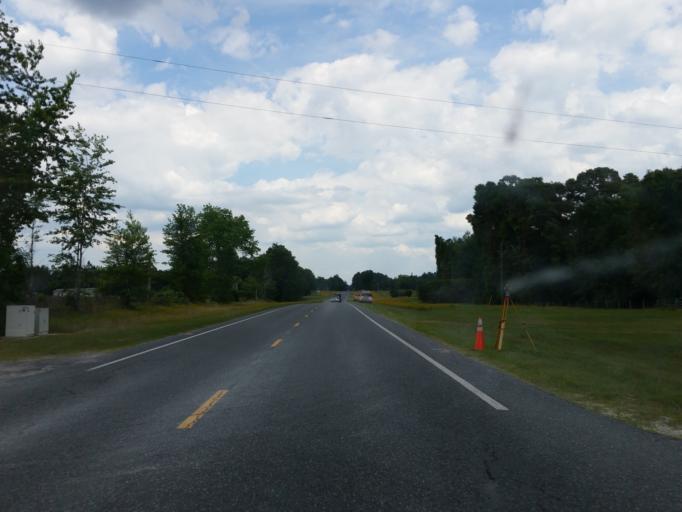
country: US
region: Florida
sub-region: Alachua County
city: High Springs
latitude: 29.9078
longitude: -82.6095
